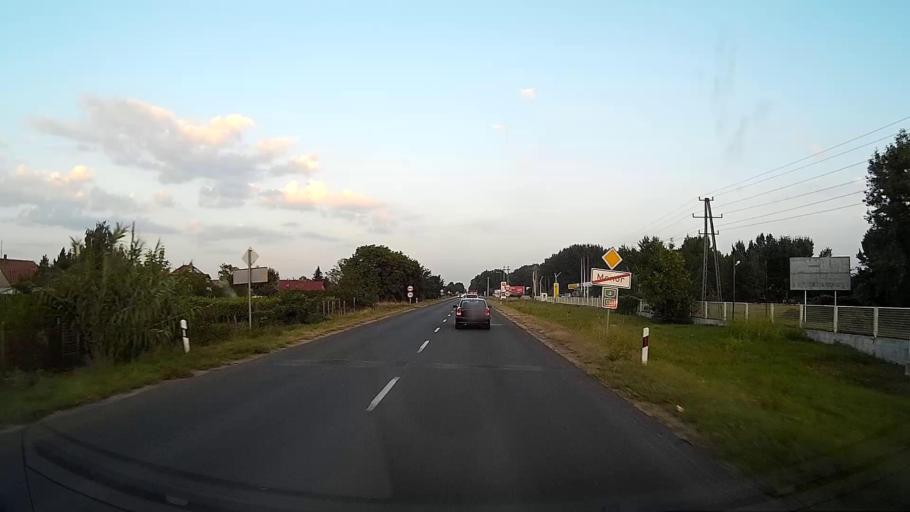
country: HU
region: Pest
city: Monor
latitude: 47.3427
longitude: 19.4244
